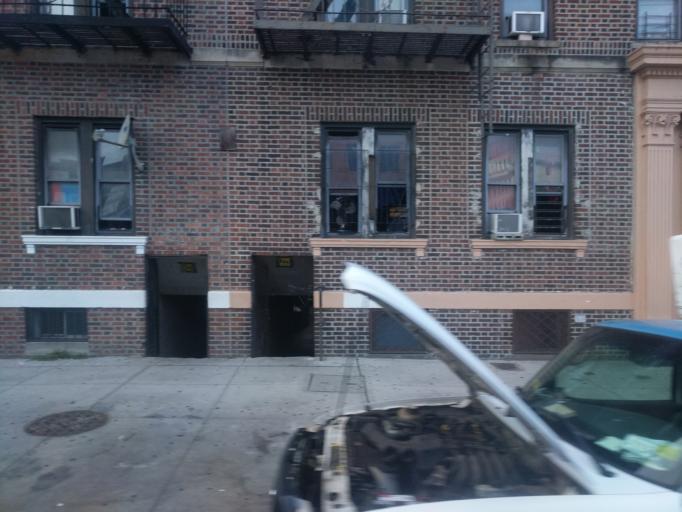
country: US
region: New York
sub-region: Queens County
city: Jamaica
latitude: 40.7058
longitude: -73.8100
